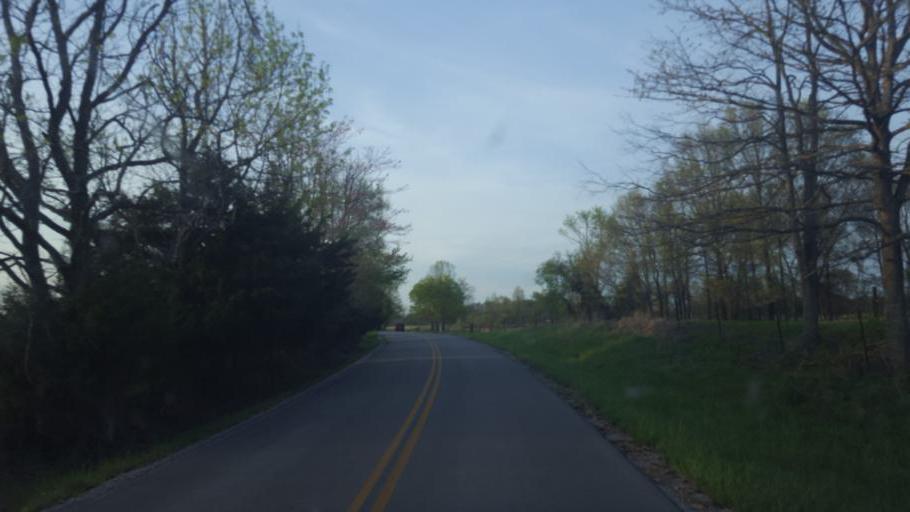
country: US
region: Kentucky
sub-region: Metcalfe County
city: Edmonton
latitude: 37.0202
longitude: -85.7228
